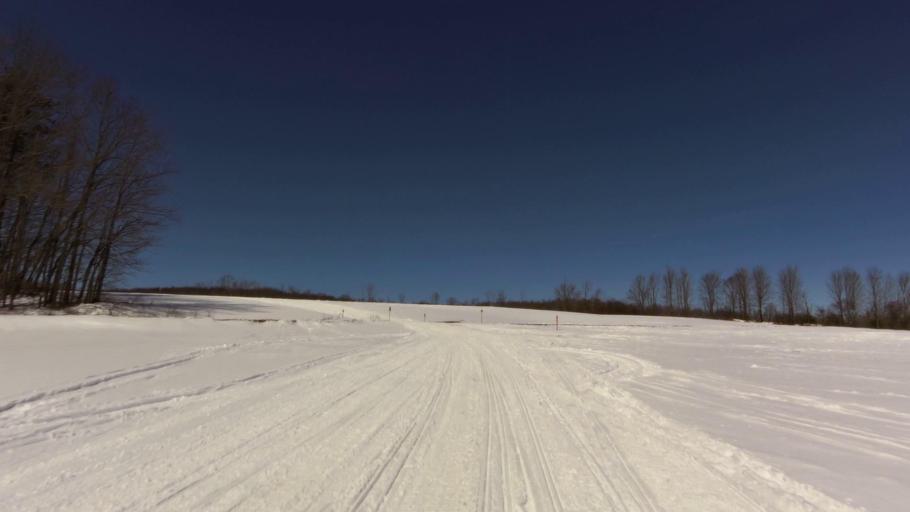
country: US
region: New York
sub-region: Allegany County
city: Houghton
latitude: 42.3992
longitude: -78.2616
